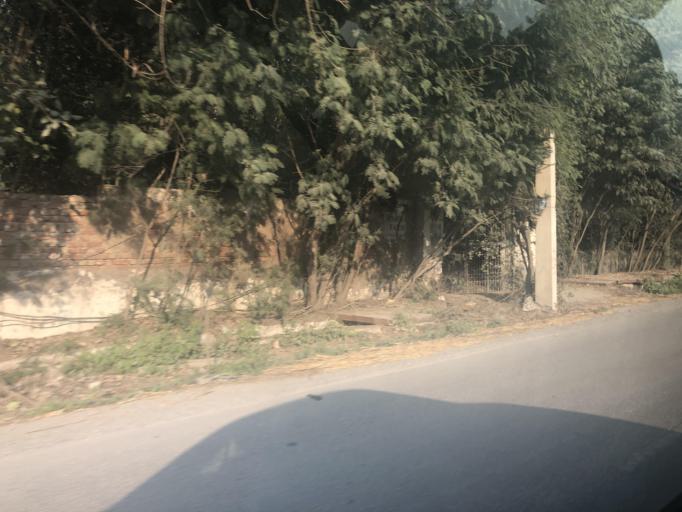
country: IN
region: Haryana
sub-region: Gurgaon
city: Gurgaon
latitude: 28.5418
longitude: 77.0193
